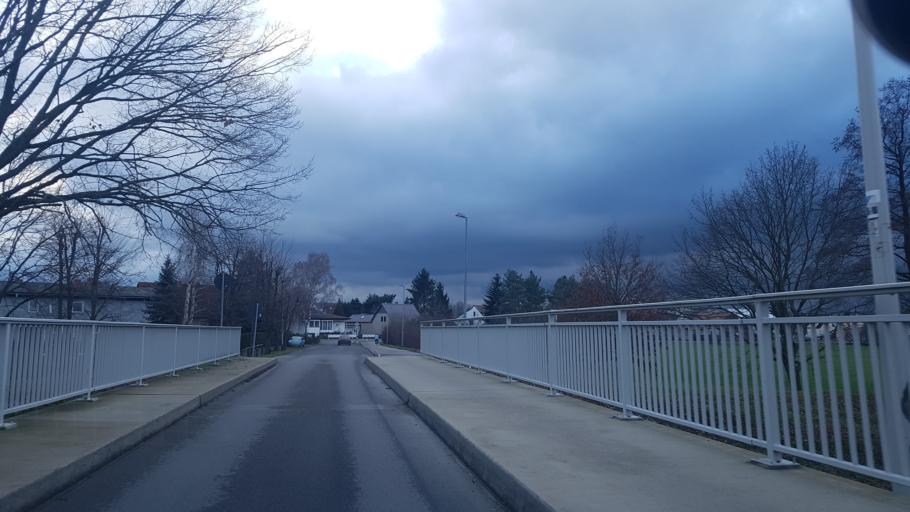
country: DE
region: Brandenburg
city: Elsterwerda
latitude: 51.4527
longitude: 13.5082
